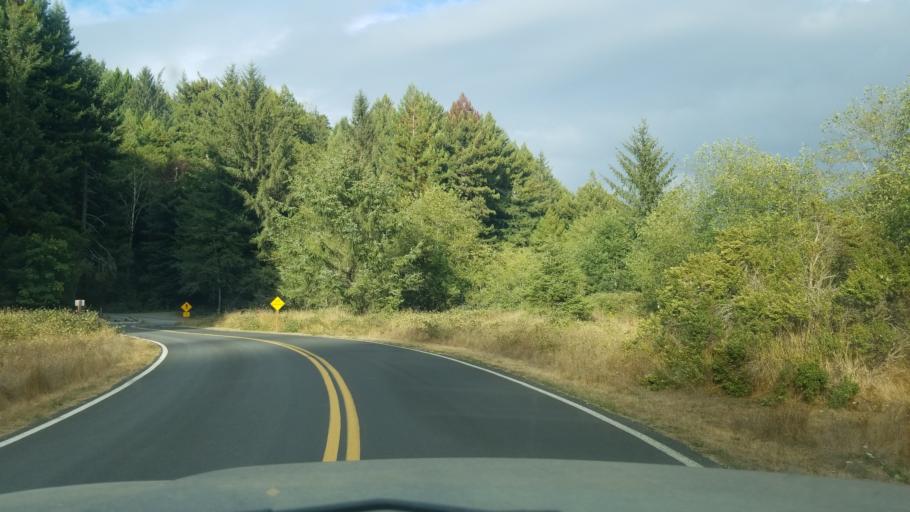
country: US
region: California
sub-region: Humboldt County
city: Westhaven-Moonstone
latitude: 41.3232
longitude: -124.0445
